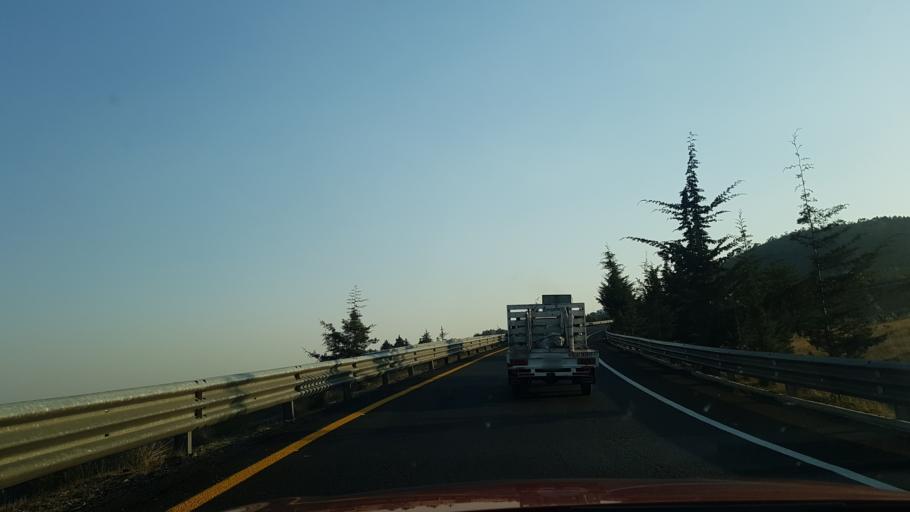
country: MX
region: Mexico
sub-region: Atlacomulco
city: San Luis Boro
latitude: 19.8338
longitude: -99.8701
